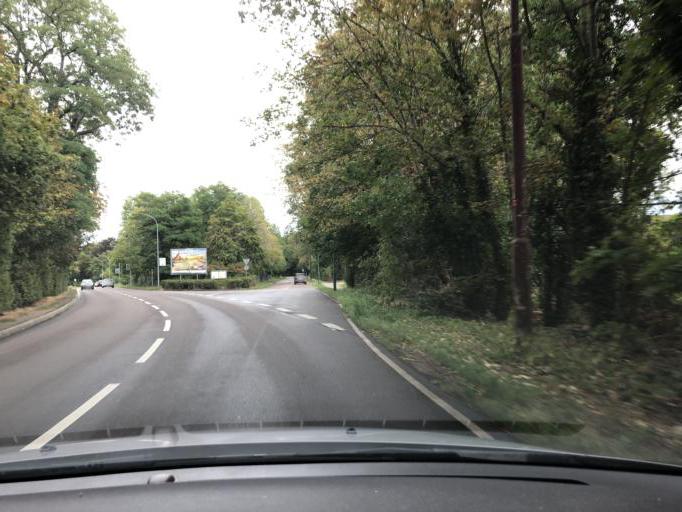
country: DE
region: Saxony-Anhalt
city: Koethen
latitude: 51.7547
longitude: 11.9498
